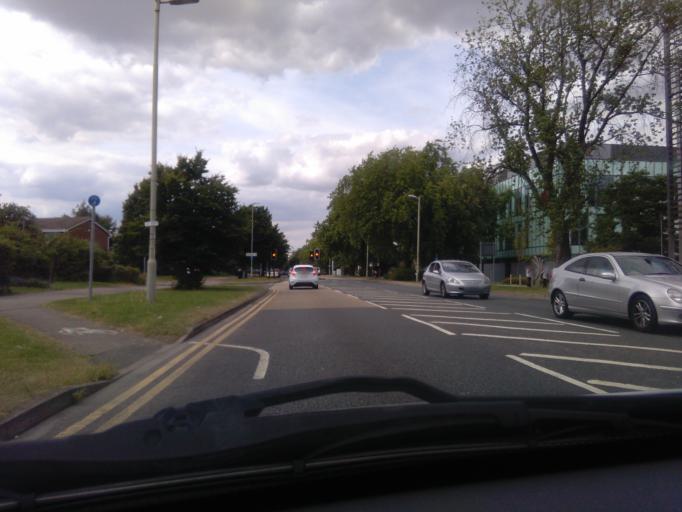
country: GB
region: England
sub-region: Bedford
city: Bedford
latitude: 52.1412
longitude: -0.4434
